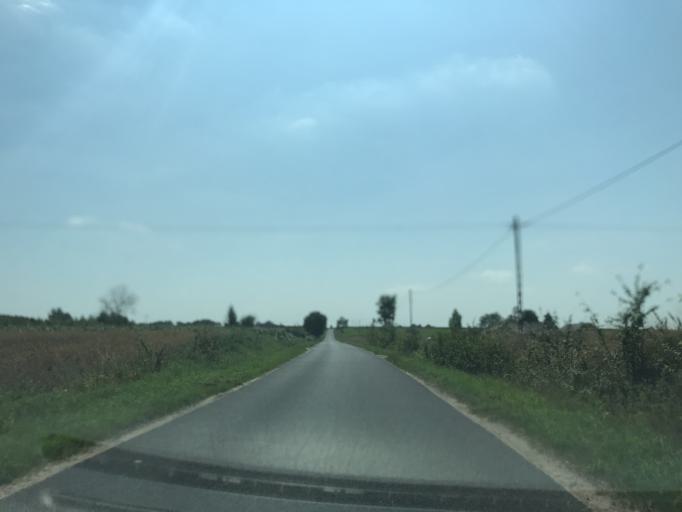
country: PL
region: Kujawsko-Pomorskie
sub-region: Powiat lipnowski
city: Chrostkowo
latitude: 52.9379
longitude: 19.1922
